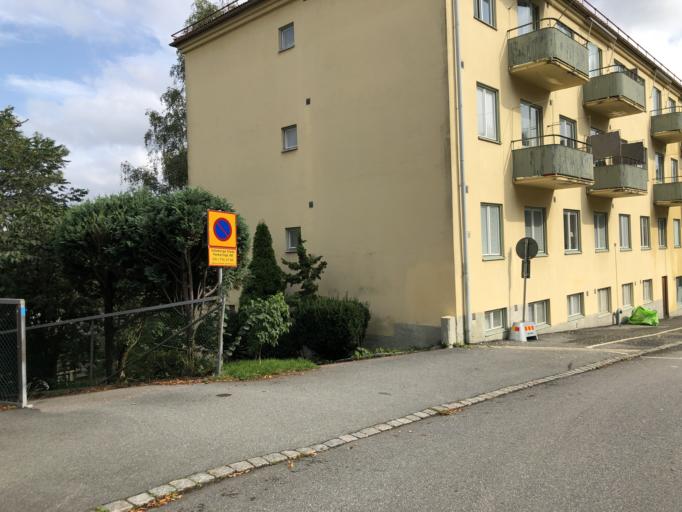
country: SE
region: Vaestra Goetaland
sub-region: Goteborg
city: Majorna
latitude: 57.6929
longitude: 11.9252
